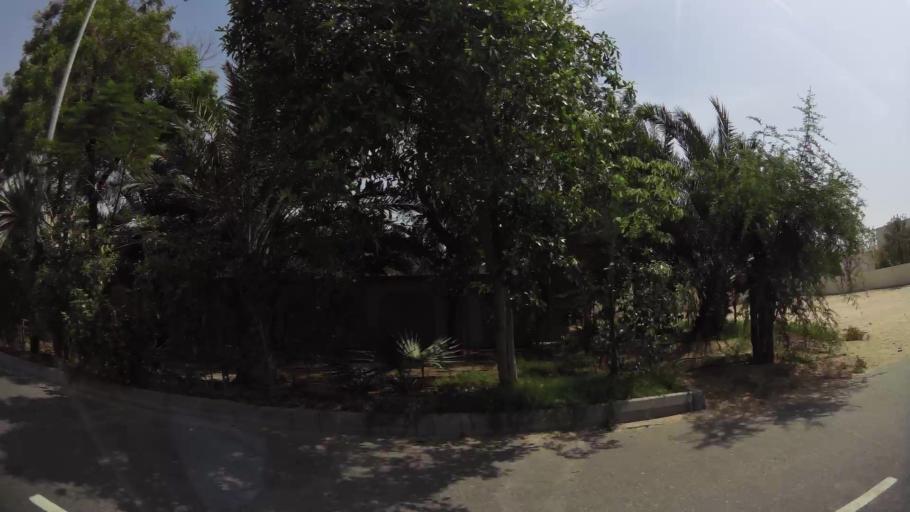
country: AE
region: Ash Shariqah
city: Sharjah
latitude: 25.2411
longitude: 55.4313
